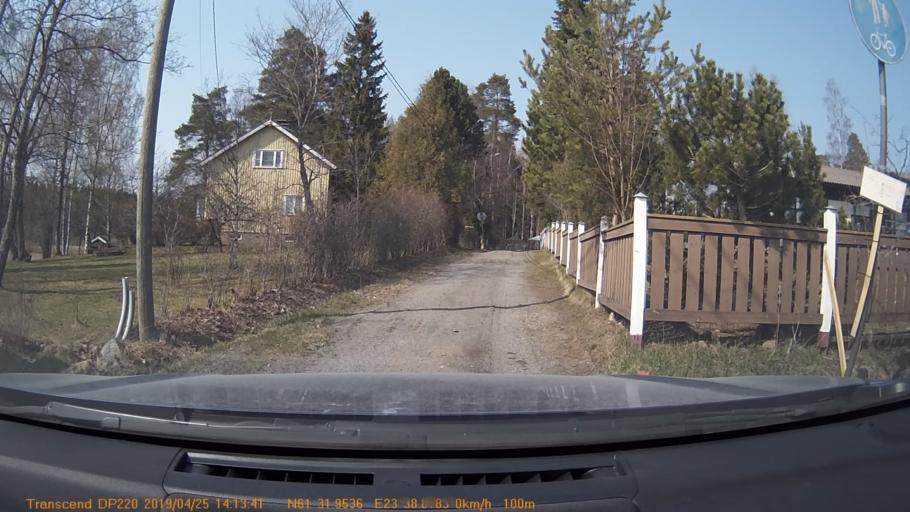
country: FI
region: Pirkanmaa
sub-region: Tampere
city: Yloejaervi
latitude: 61.5325
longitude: 23.6470
